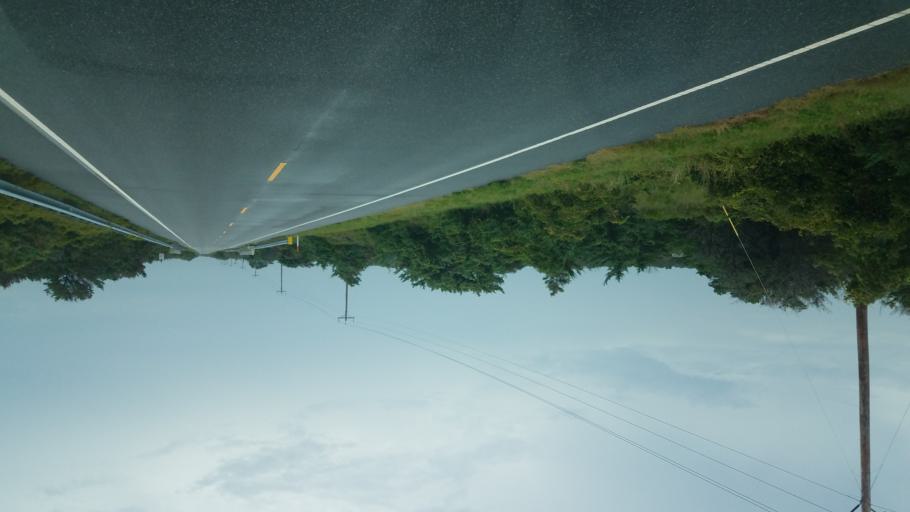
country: US
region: North Carolina
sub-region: Dare County
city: Buxton
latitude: 35.1400
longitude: -75.8948
